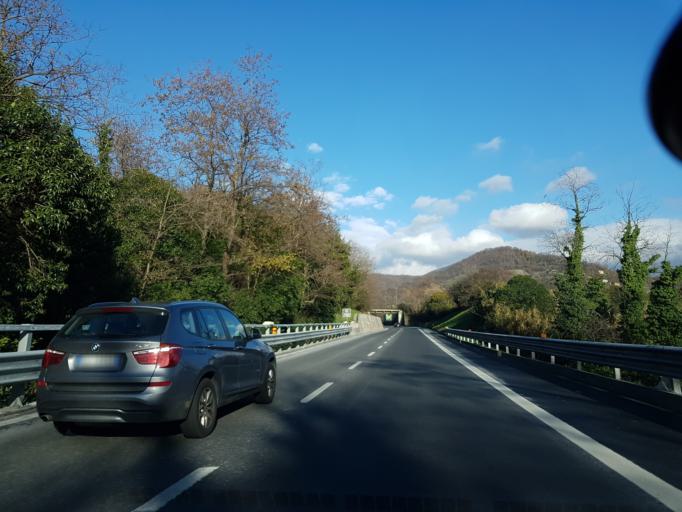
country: IT
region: Liguria
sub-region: Provincia di Genova
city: Manesseno
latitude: 44.4797
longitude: 8.9157
